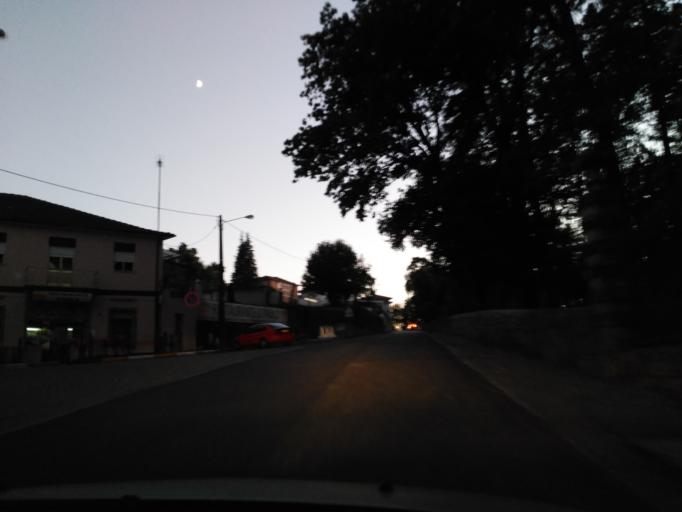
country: PT
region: Braga
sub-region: Braga
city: Adaufe
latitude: 41.5534
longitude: -8.3743
